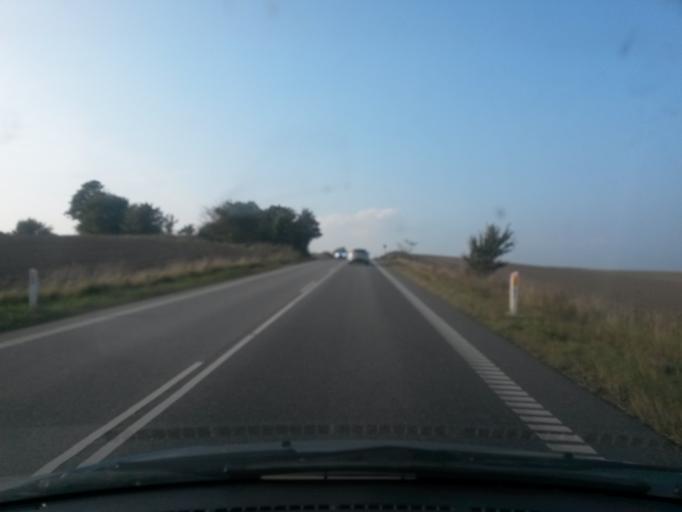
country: DK
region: Central Jutland
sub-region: Syddjurs Kommune
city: Hornslet
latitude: 56.3745
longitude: 10.3108
